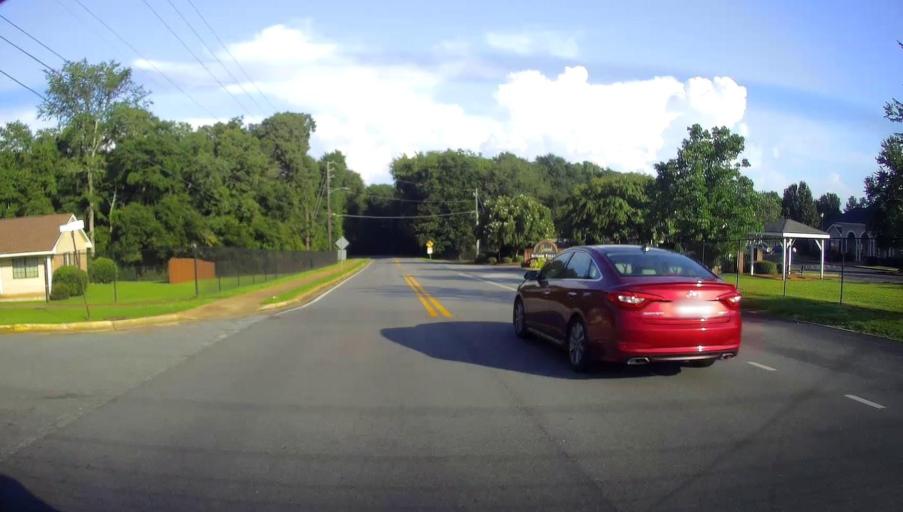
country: US
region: Georgia
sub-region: Houston County
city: Perry
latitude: 32.4694
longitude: -83.7356
